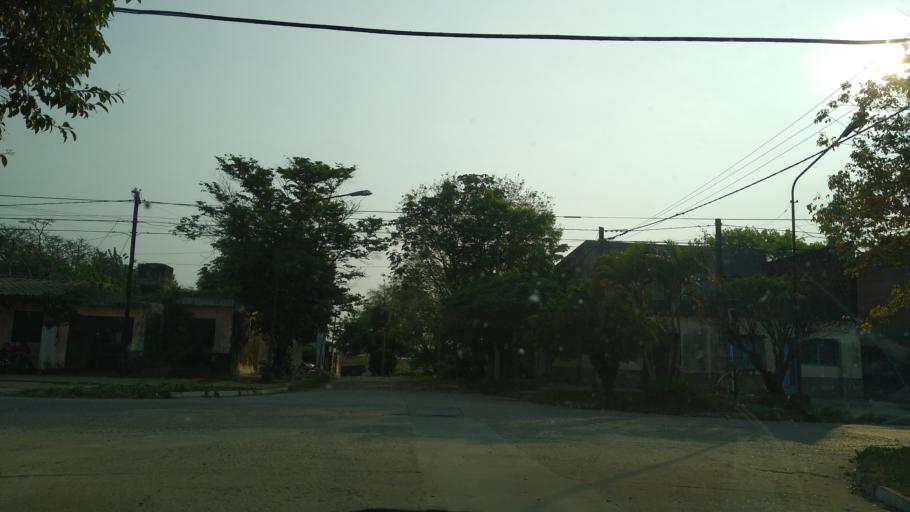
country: AR
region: Chaco
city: Barranqueras
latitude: -27.4790
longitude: -58.9517
